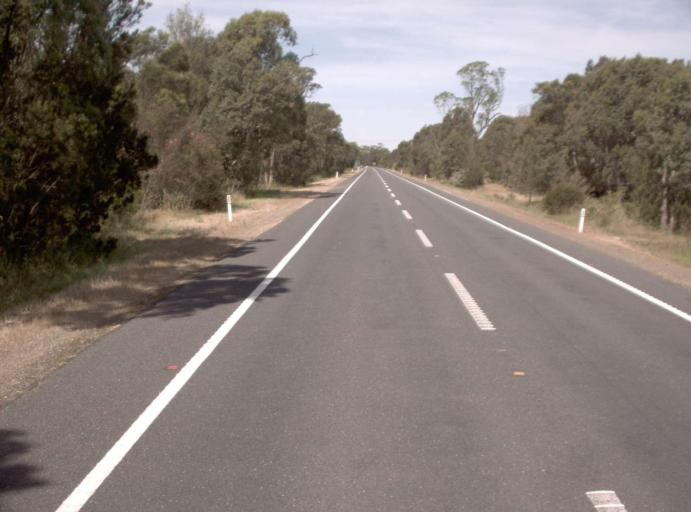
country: AU
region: Victoria
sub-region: East Gippsland
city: Bairnsdale
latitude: -37.8495
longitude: 147.5576
